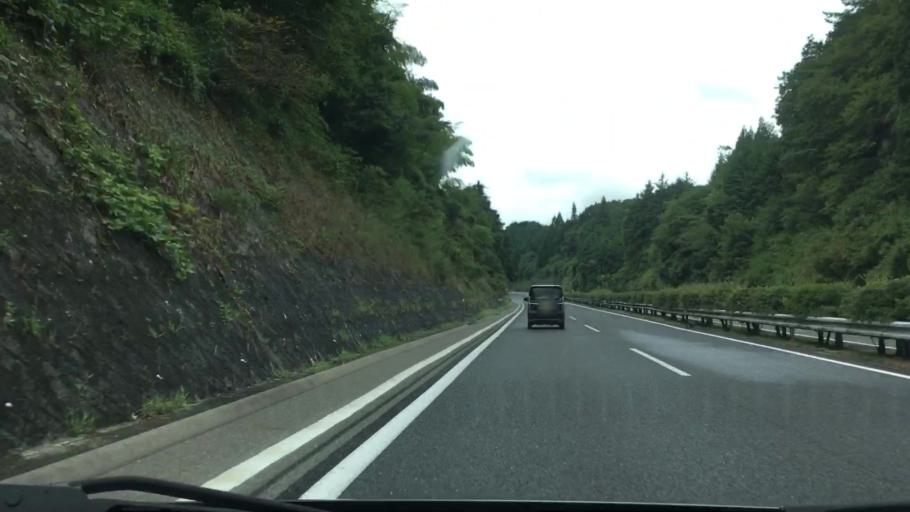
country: JP
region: Okayama
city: Tsuyama
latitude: 35.0597
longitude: 133.8318
